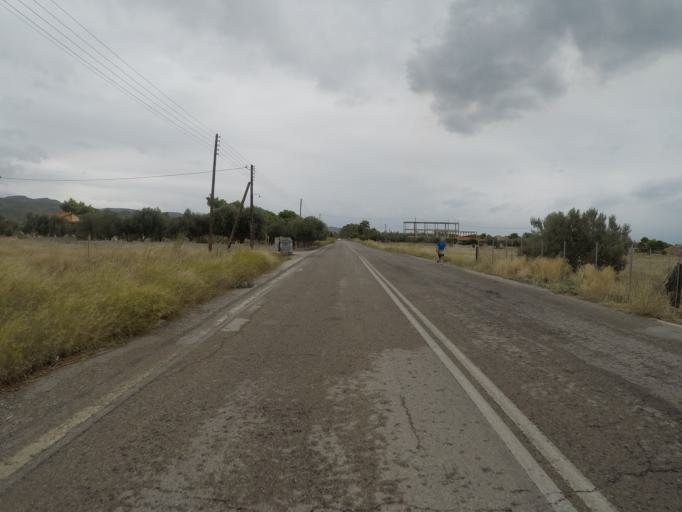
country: GR
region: Peloponnese
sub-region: Nomos Korinthias
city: Isthmia
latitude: 37.9214
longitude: 23.0344
